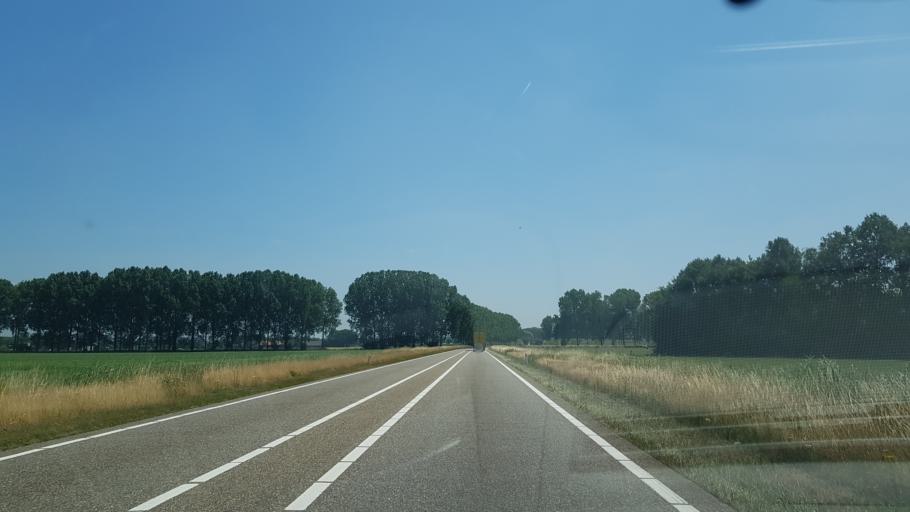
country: NL
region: North Brabant
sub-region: Gemeente Laarbeek
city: Aarle-Rixtel
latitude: 51.5474
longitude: 5.6430
